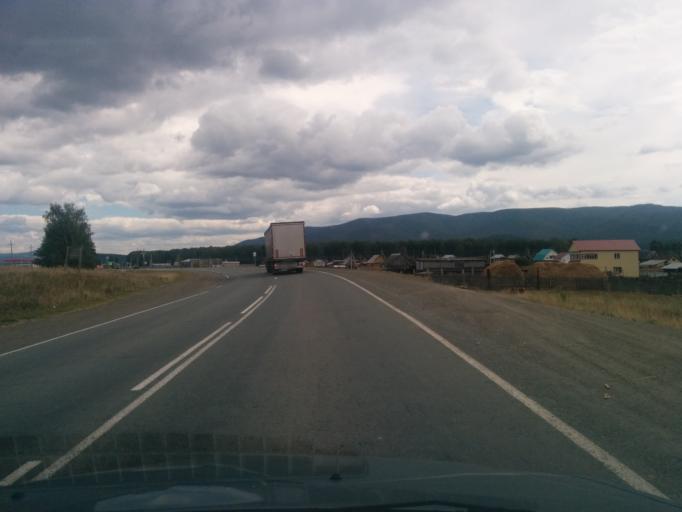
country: RU
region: Bashkortostan
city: Lomovka
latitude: 53.8840
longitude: 58.1000
